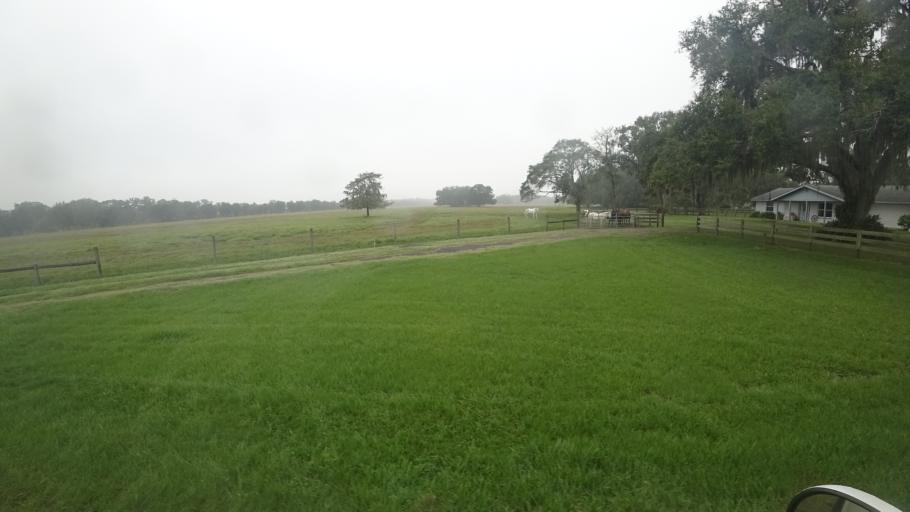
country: US
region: Florida
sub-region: Sarasota County
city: Lake Sarasota
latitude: 27.2917
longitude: -82.2348
